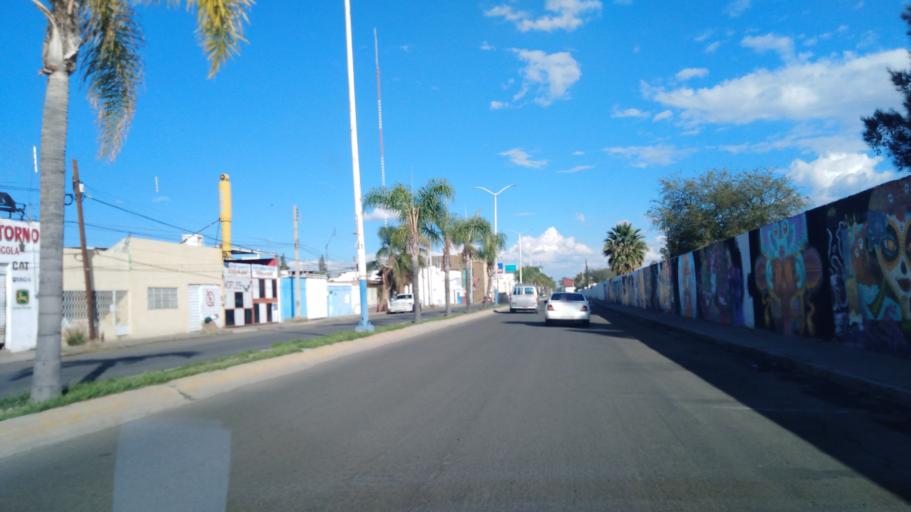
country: MX
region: Durango
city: Victoria de Durango
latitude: 24.0300
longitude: -104.6397
